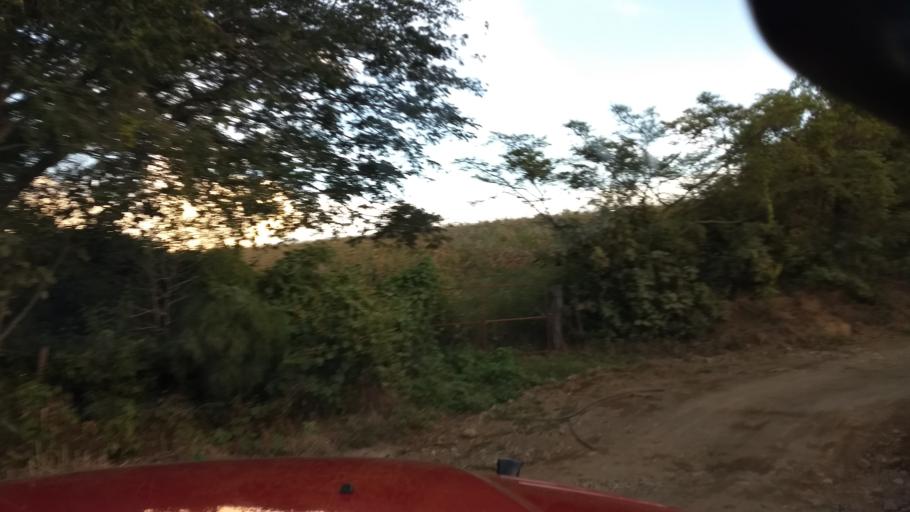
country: MX
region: Colima
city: Suchitlan
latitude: 19.4888
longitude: -103.7896
